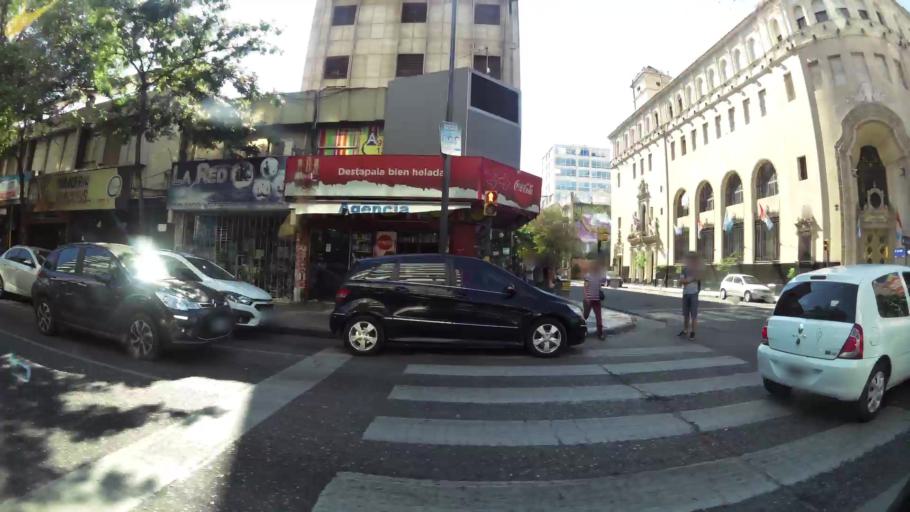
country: AR
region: Cordoba
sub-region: Departamento de Capital
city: Cordoba
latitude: -31.4163
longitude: -64.1872
